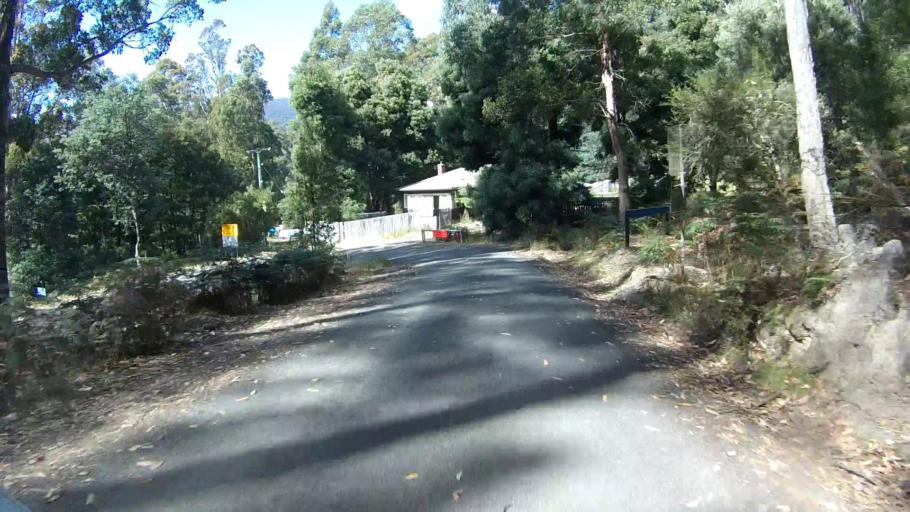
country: AU
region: Tasmania
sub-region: Derwent Valley
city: New Norfolk
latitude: -42.6831
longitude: 146.7151
